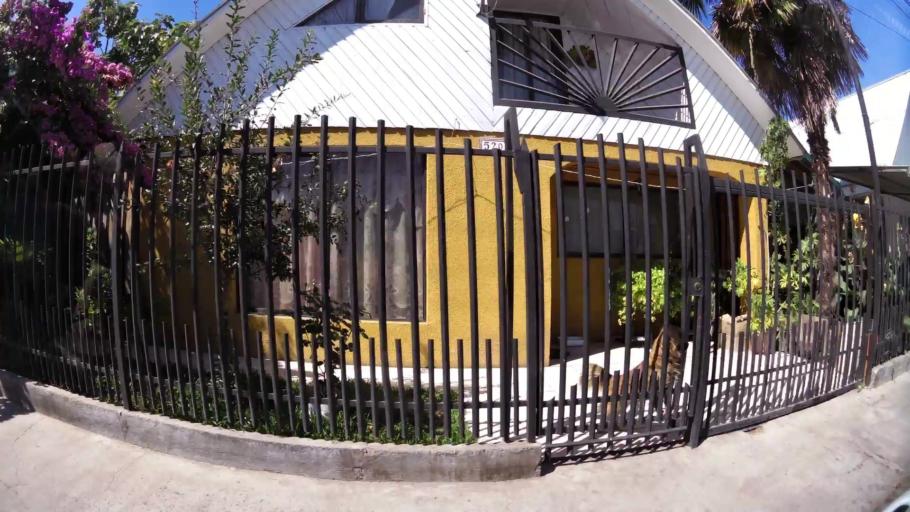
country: CL
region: Maule
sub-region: Provincia de Curico
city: Curico
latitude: -34.9681
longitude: -71.2429
